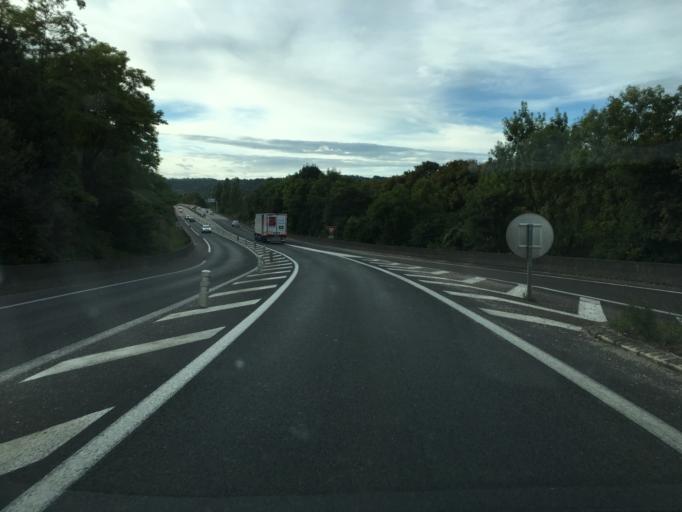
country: FR
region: Bourgogne
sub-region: Departement de la Cote-d'Or
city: Plombieres-les-Dijon
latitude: 47.3335
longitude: 4.9767
